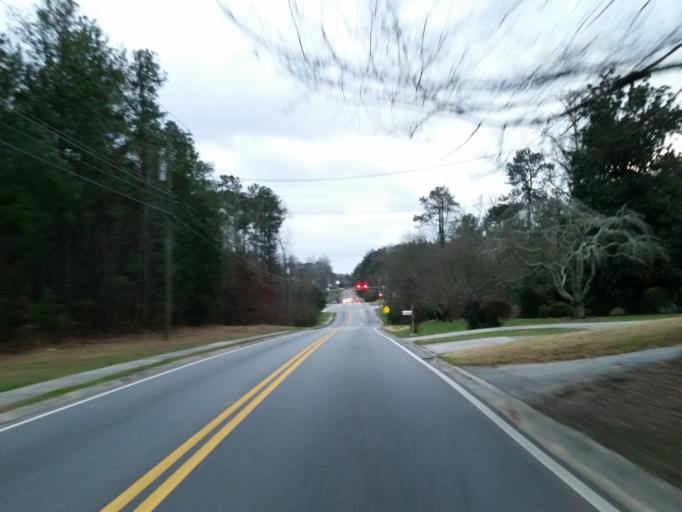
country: US
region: Georgia
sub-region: Cobb County
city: Fair Oaks
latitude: 33.8833
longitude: -84.5797
